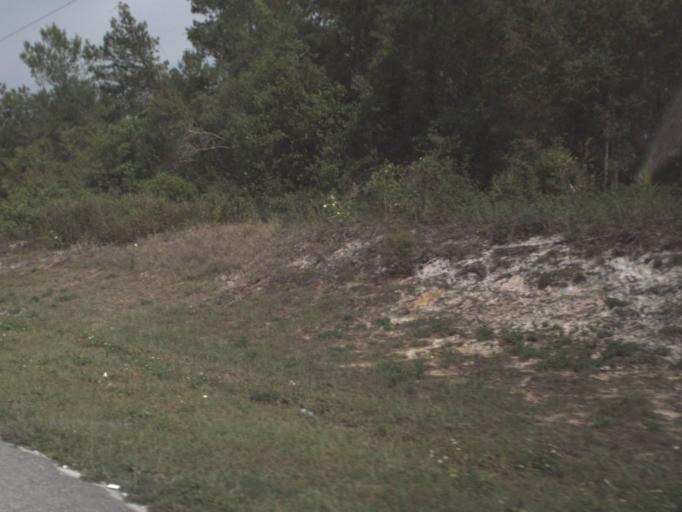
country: US
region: Florida
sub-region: Lake County
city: Astor
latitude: 29.2962
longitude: -81.6614
